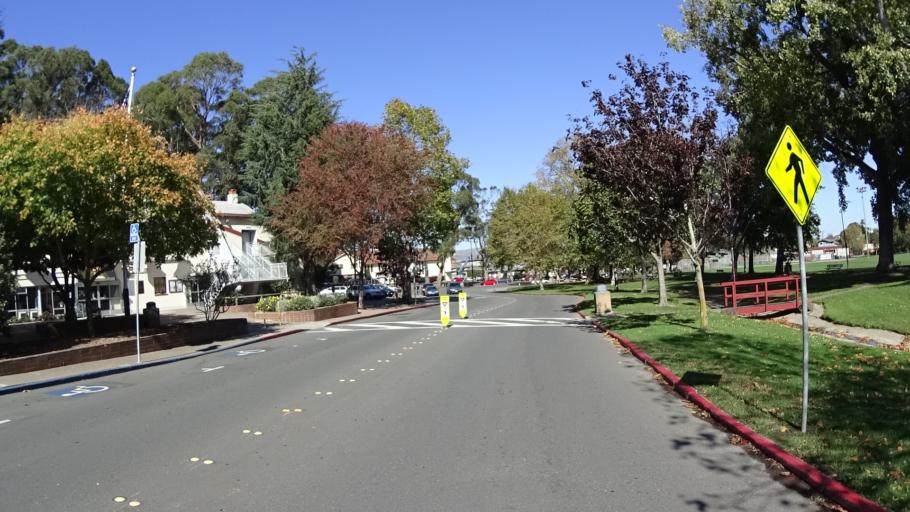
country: US
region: California
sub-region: San Mateo County
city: San Bruno
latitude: 37.6147
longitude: -122.4153
